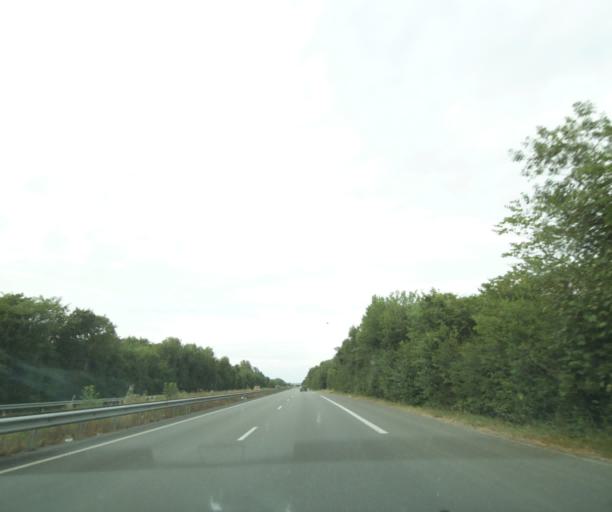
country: FR
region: Poitou-Charentes
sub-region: Departement de la Charente-Maritime
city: Dompierre-sur-Mer
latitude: 46.1855
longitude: -1.0774
